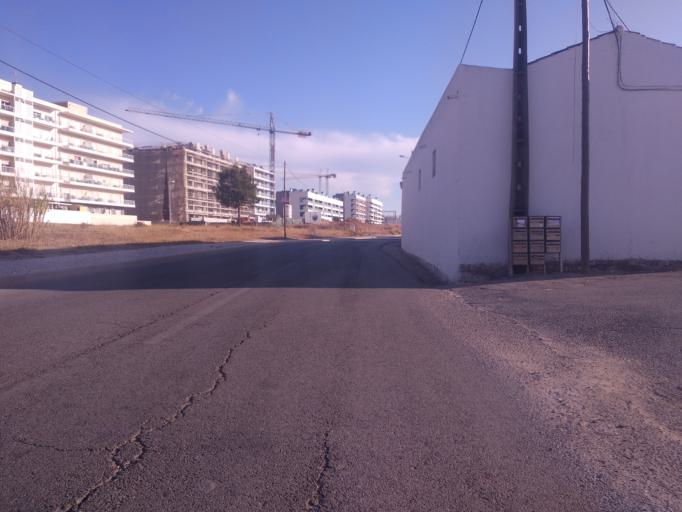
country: PT
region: Faro
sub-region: Faro
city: Faro
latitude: 37.0337
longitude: -7.9399
